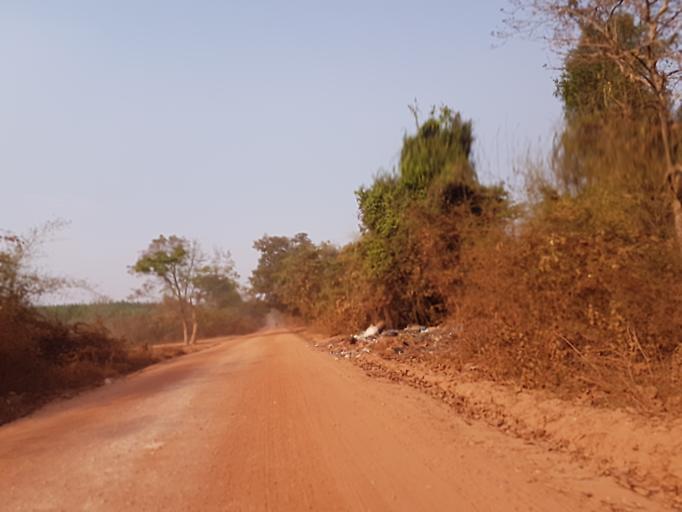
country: TH
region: Nong Khai
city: Phon Phisai
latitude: 18.0084
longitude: 102.9091
